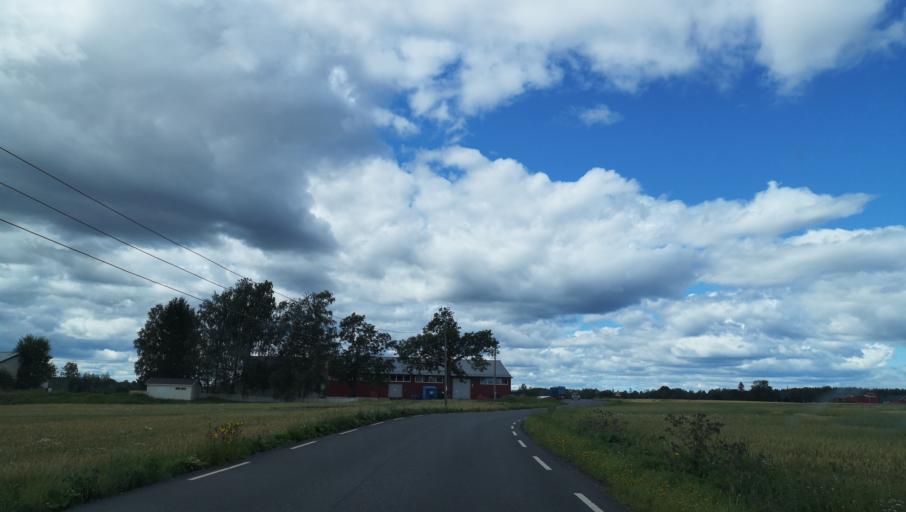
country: NO
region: Akershus
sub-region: Ski
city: Ski
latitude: 59.7084
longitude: 10.8869
